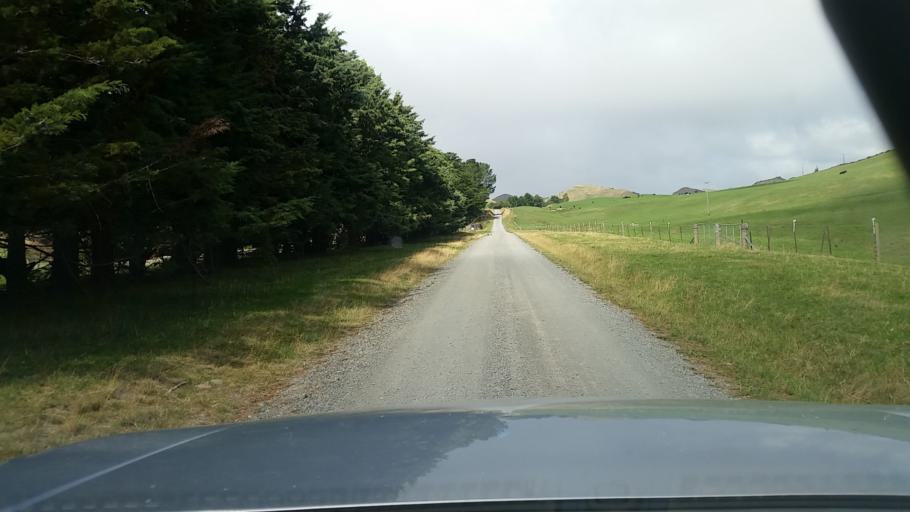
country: NZ
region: Marlborough
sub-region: Marlborough District
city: Blenheim
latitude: -41.7448
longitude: 173.8937
